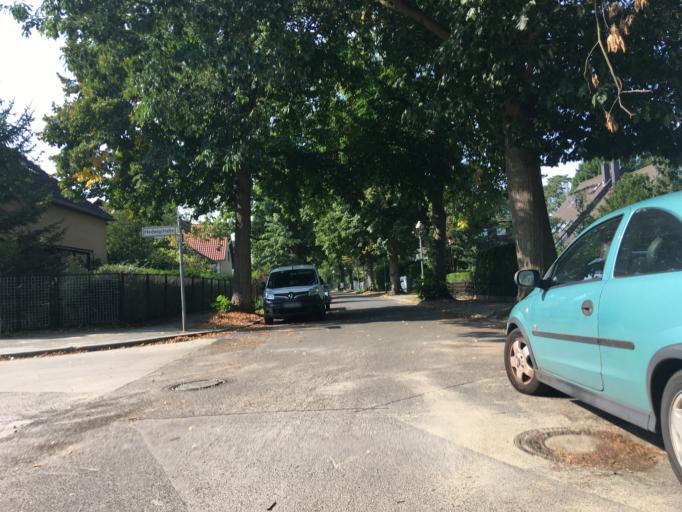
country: DE
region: Brandenburg
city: Glienicke
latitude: 52.6244
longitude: 13.3297
